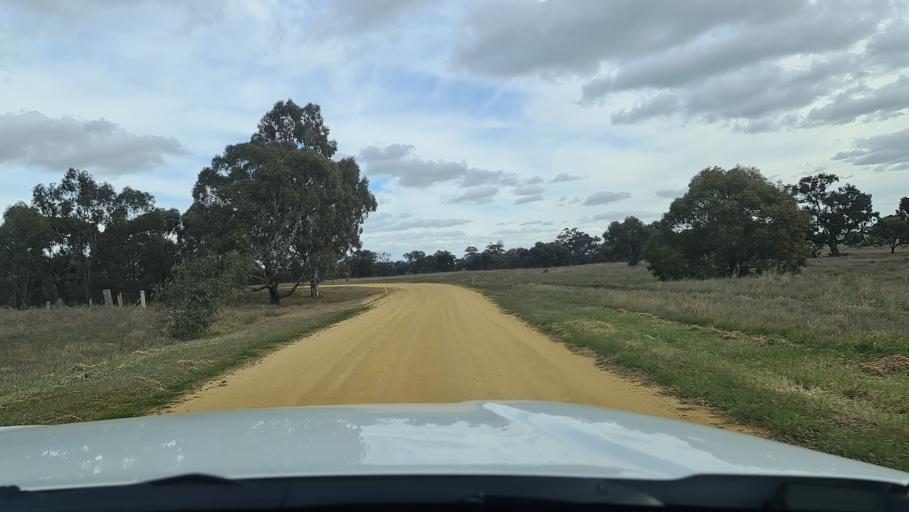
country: AU
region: Victoria
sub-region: Horsham
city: Horsham
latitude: -36.6200
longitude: 142.4214
